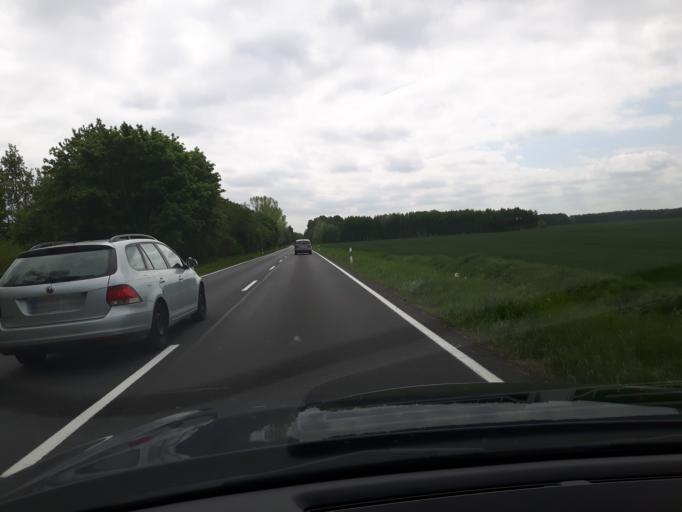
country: DE
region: Mecklenburg-Vorpommern
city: Ostseebad Dierhagen
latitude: 54.2370
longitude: 12.3629
